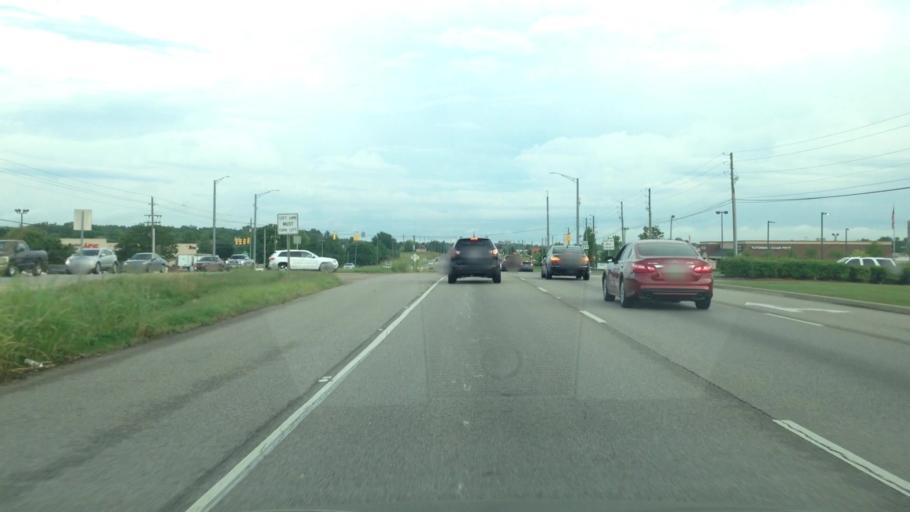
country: US
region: Alabama
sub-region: Montgomery County
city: Pike Road
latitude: 32.3374
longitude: -86.1794
